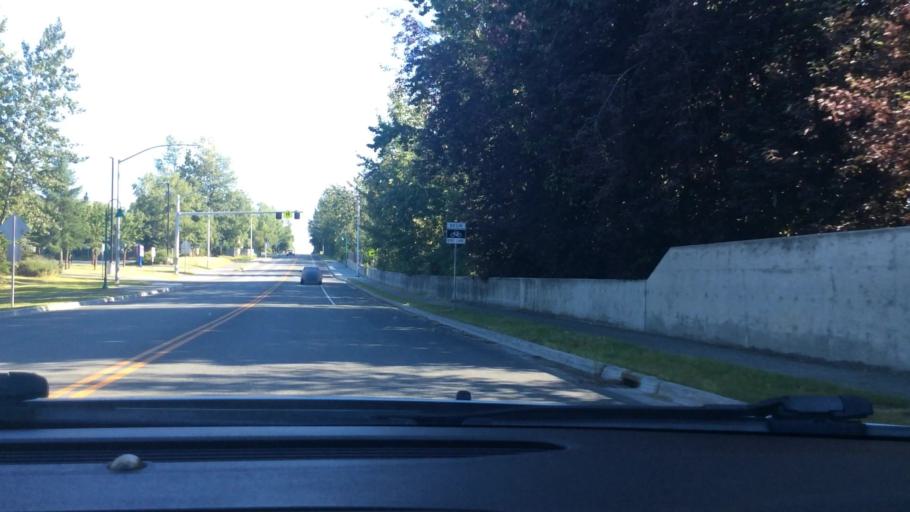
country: US
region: Alaska
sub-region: Anchorage Municipality
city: Anchorage
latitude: 61.1944
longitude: -149.7634
